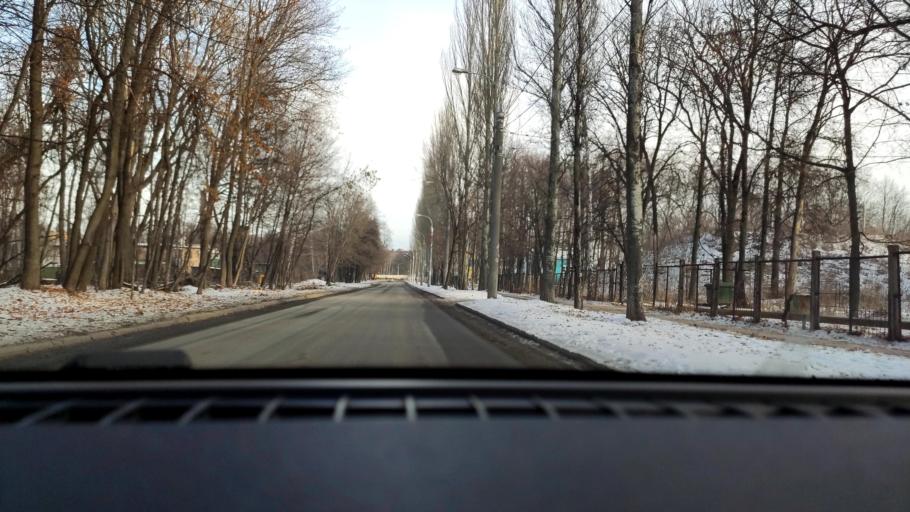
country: RU
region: Samara
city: Petra-Dubrava
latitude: 53.3059
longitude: 50.2747
